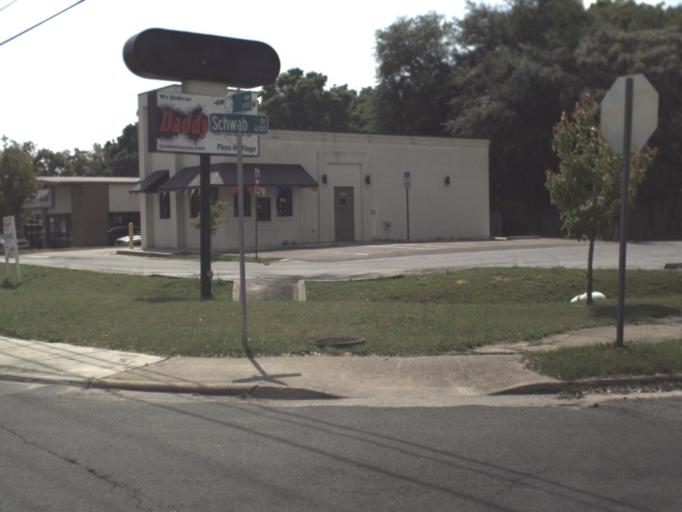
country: US
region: Florida
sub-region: Escambia County
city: Ferry Pass
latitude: 30.4863
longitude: -87.1995
